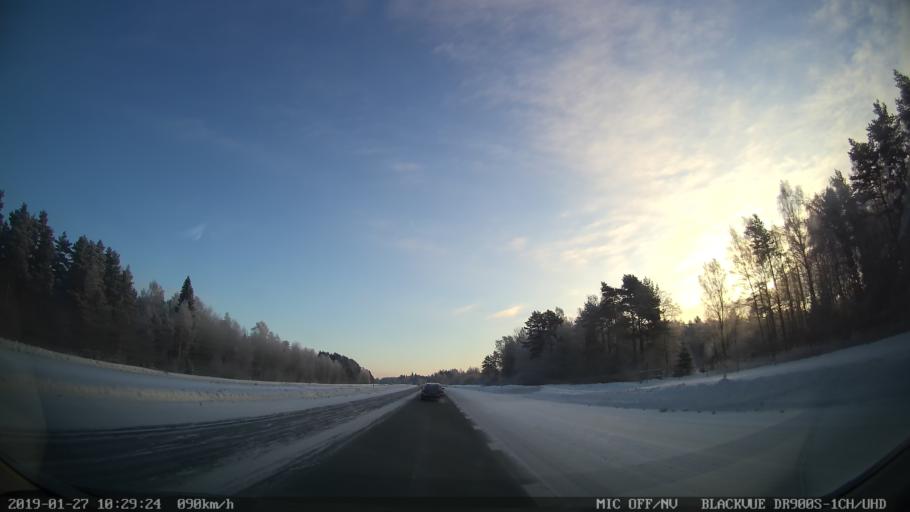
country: EE
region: Harju
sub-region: Raasiku vald
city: Raasiku
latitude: 59.4360
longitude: 25.1655
